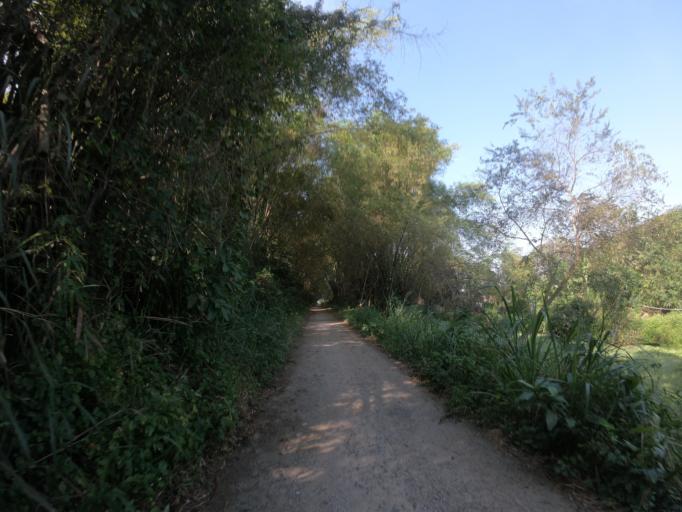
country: TH
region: Chiang Mai
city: Chiang Mai
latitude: 18.7397
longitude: 98.9858
